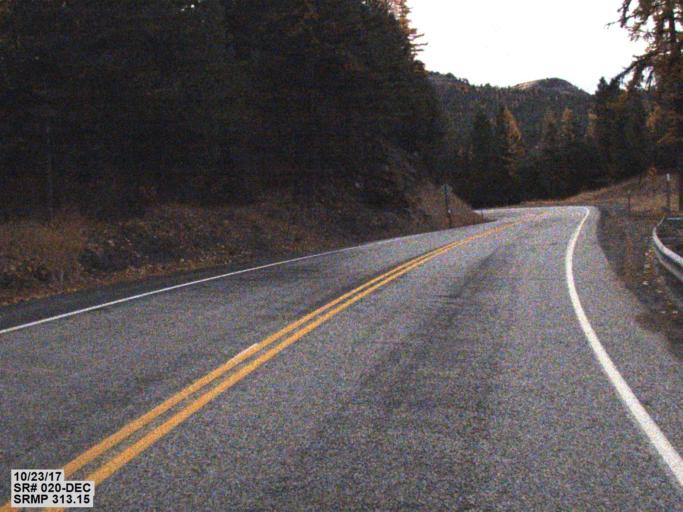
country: US
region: Washington
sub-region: Ferry County
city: Republic
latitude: 48.6126
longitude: -118.5752
